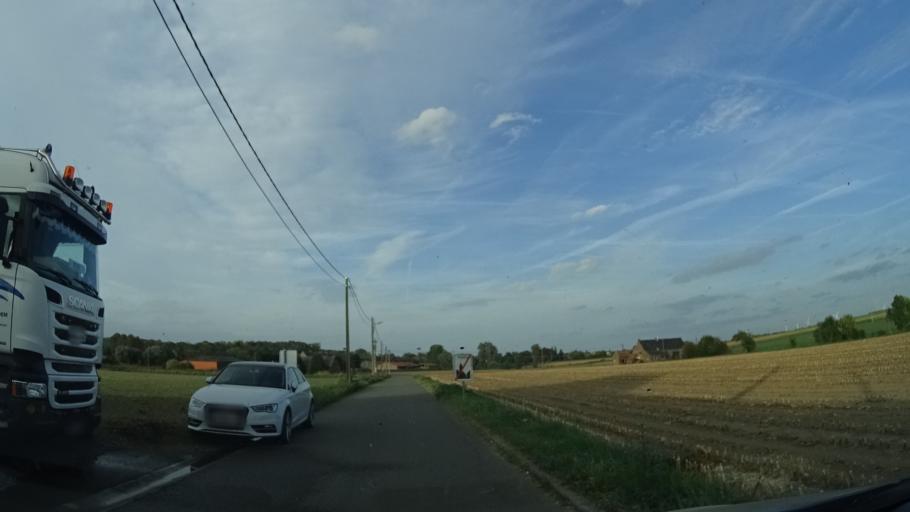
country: BE
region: Wallonia
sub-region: Province du Hainaut
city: Peruwelz
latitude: 50.5906
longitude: 3.5883
